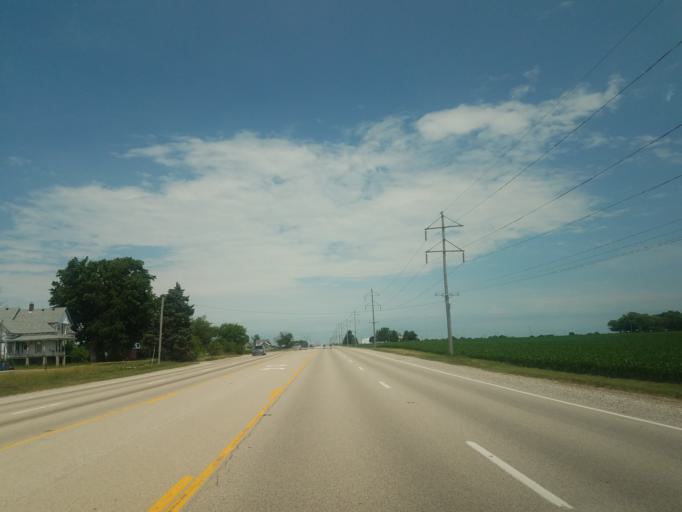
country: US
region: Illinois
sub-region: McLean County
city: Downs
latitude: 40.4384
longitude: -88.9016
